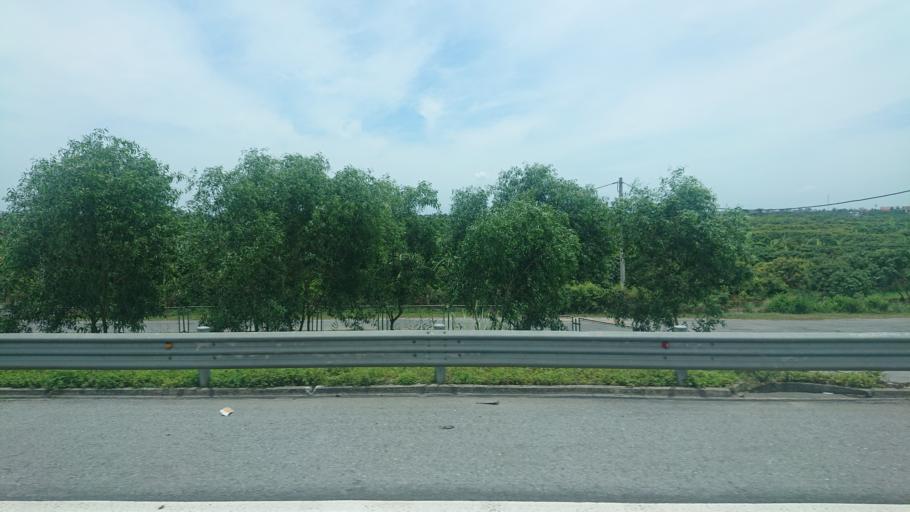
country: VN
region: Hai Duong
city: Tu Ky
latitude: 20.8240
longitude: 106.4679
